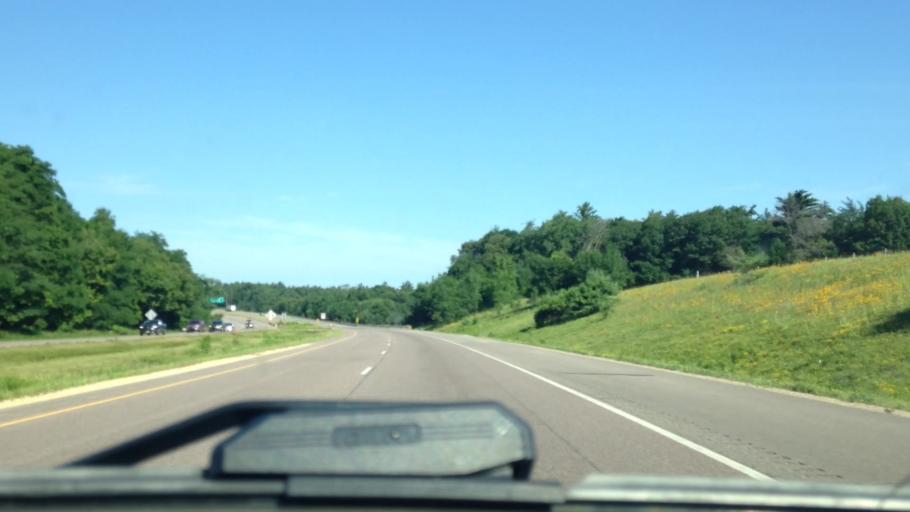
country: US
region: Wisconsin
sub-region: Eau Claire County
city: Altoona
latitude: 44.7642
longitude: -91.4055
